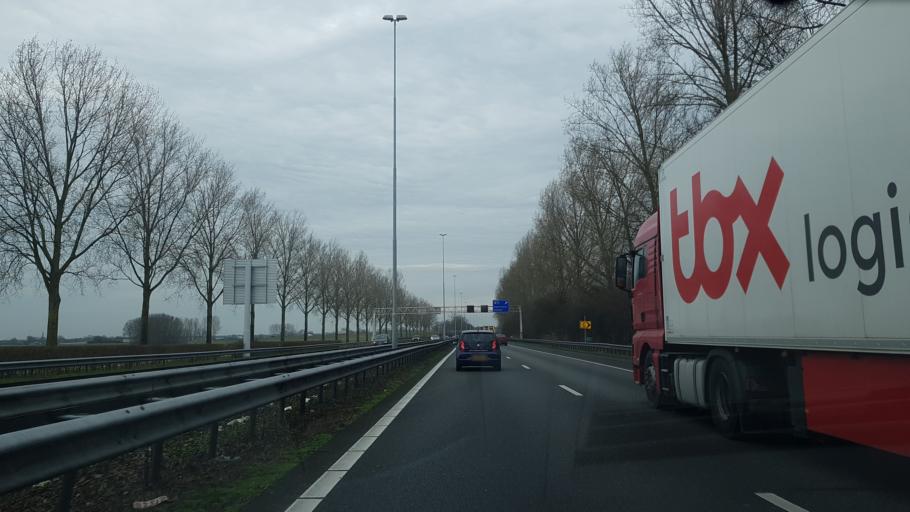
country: NL
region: North Brabant
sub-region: Gemeente Oosterhout
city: Oosterhout
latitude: 51.6564
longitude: 4.8817
